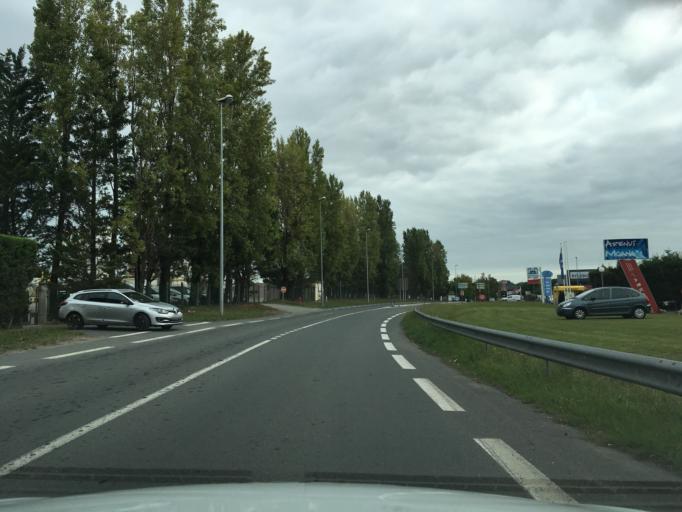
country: FR
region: Aquitaine
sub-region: Departement des Pyrenees-Atlantiques
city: Bayonne
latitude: 43.5003
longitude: -1.4972
